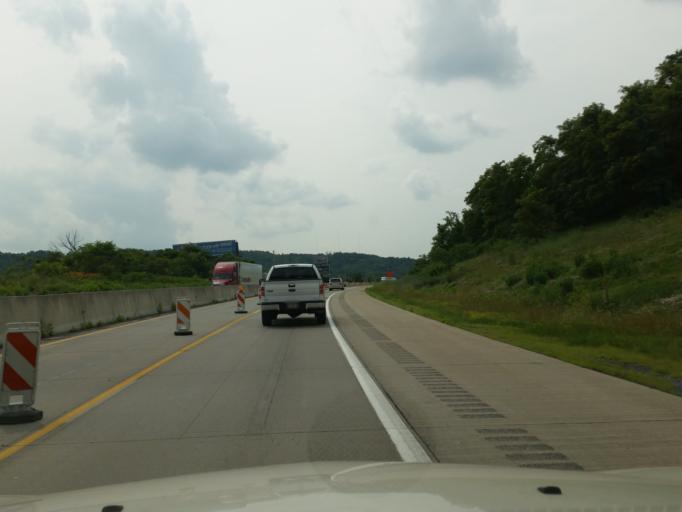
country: US
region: Pennsylvania
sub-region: Mifflin County
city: Lewistown
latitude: 40.5787
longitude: -77.5468
